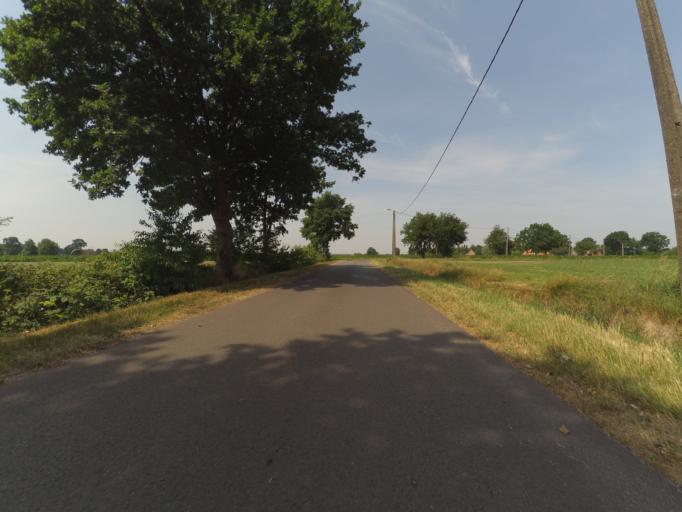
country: BE
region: Flanders
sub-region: Provincie Antwerpen
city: Essen
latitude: 51.4467
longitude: 4.4057
